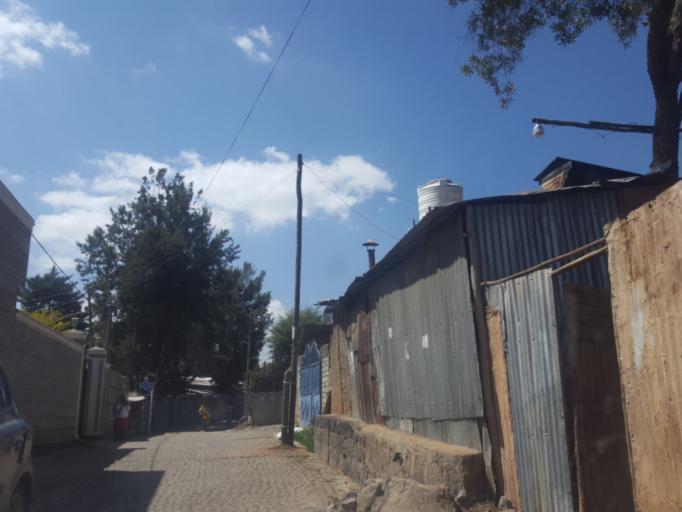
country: ET
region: Adis Abeba
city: Addis Ababa
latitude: 9.0515
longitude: 38.7322
